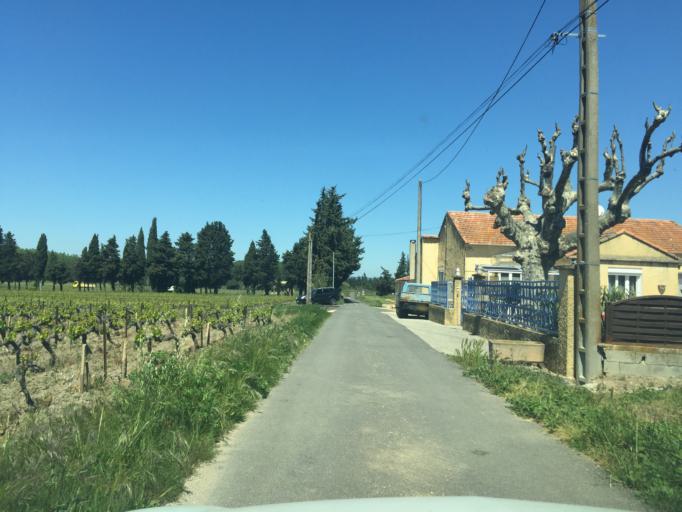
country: FR
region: Provence-Alpes-Cote d'Azur
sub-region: Departement du Vaucluse
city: Caderousse
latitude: 44.0906
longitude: 4.7939
